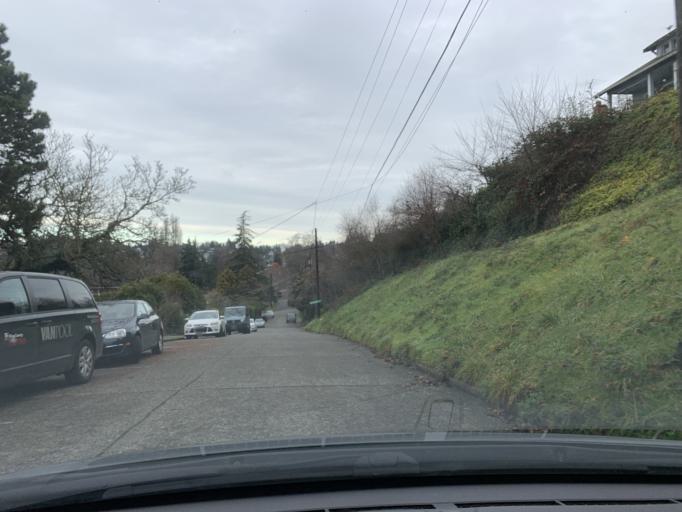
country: US
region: Washington
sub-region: King County
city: White Center
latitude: 47.5534
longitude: -122.3923
